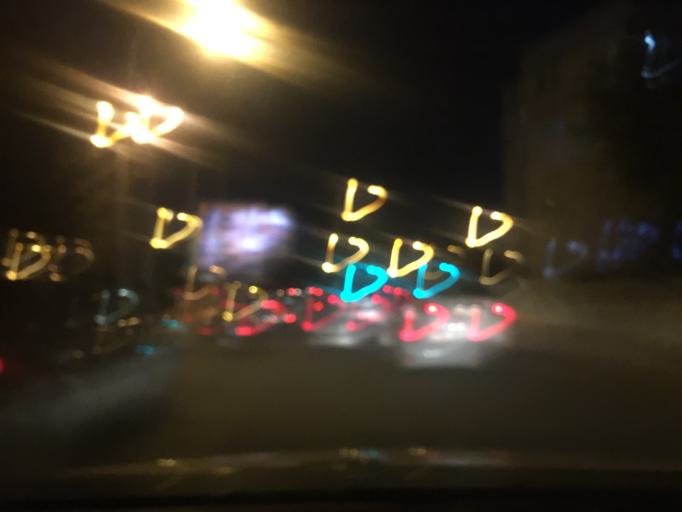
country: JO
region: Amman
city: Amman
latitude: 31.9794
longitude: 35.9166
